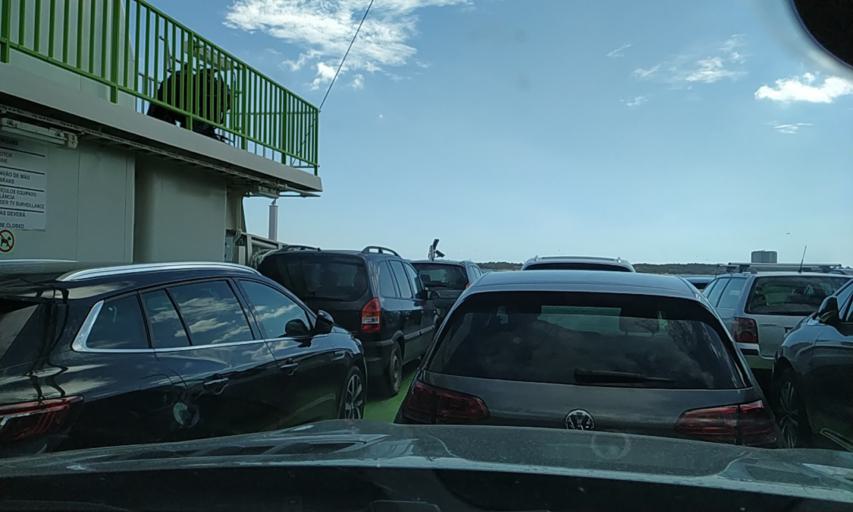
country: PT
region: Setubal
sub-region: Setubal
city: Setubal
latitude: 38.5011
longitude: -8.8869
